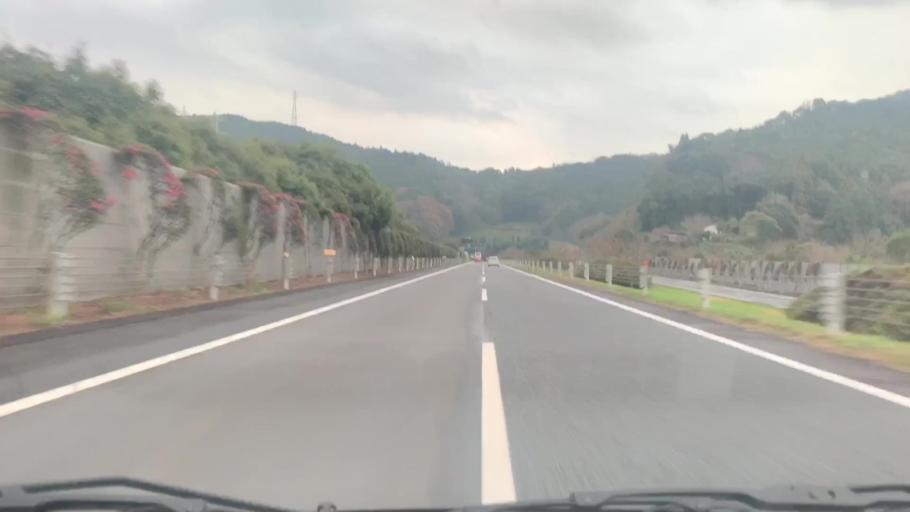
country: JP
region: Nagasaki
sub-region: Isahaya-shi
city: Isahaya
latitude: 32.8778
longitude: 129.9969
